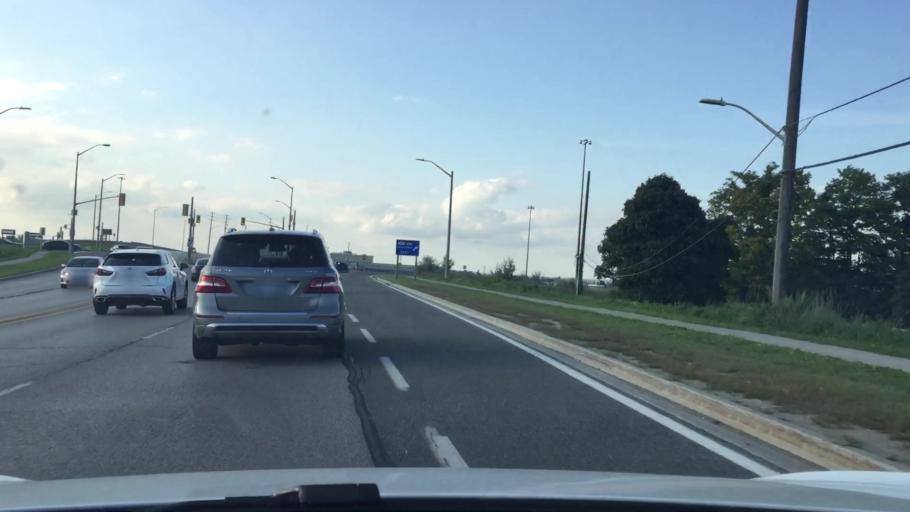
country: CA
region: Ontario
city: Markham
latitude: 43.8481
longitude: -79.3061
